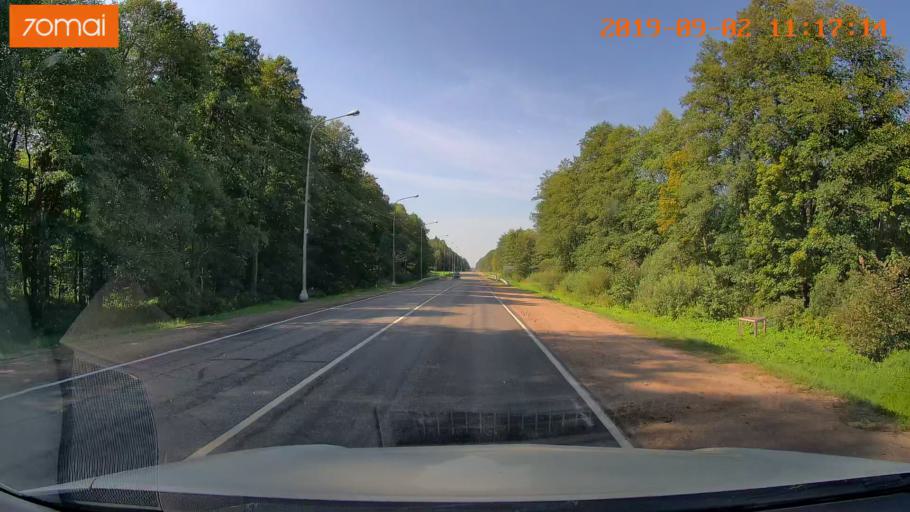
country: RU
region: Smolensk
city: Yekimovichi
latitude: 54.0630
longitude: 33.1229
